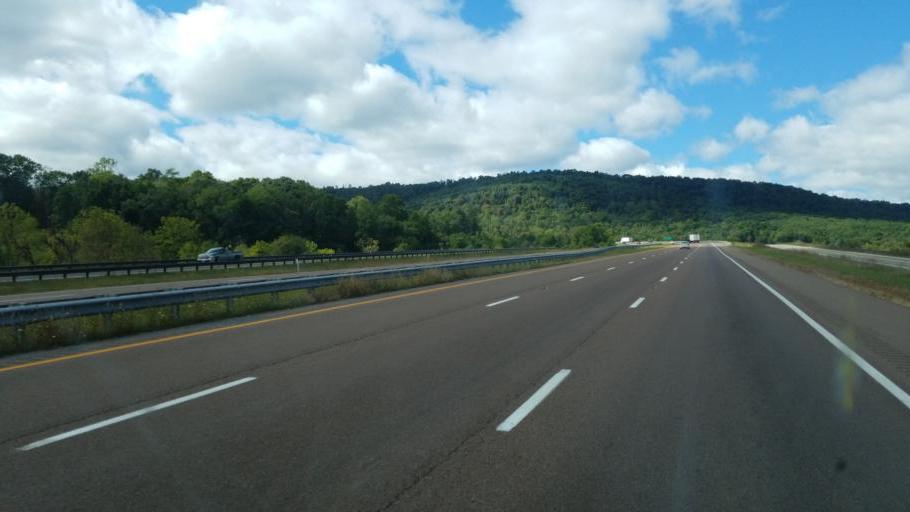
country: US
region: Maryland
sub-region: Allegany County
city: Cumberland
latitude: 39.7112
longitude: -78.6037
